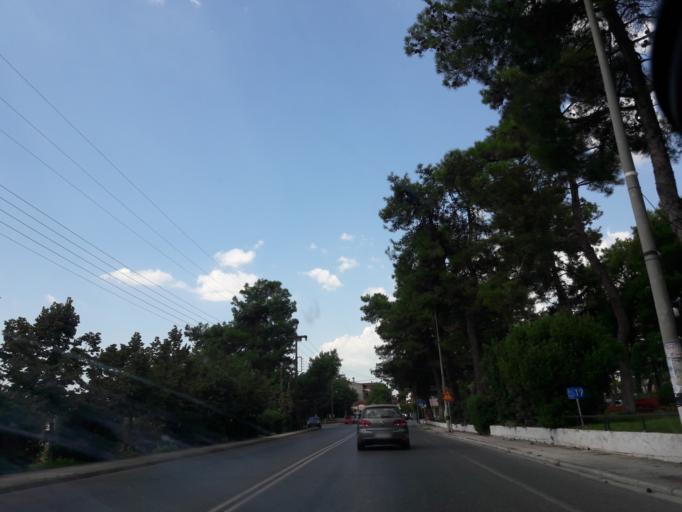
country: GR
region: Central Macedonia
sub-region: Nomos Thessalonikis
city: Thermi
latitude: 40.5235
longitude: 23.0517
